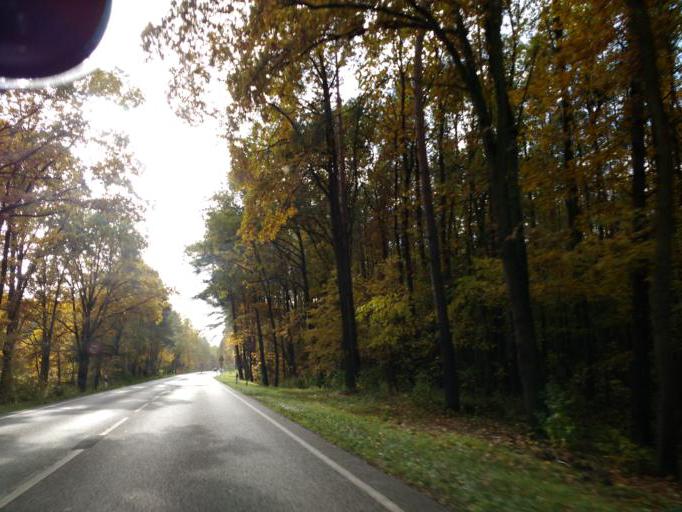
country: DE
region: Brandenburg
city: Petershagen
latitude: 52.5186
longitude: 13.8095
